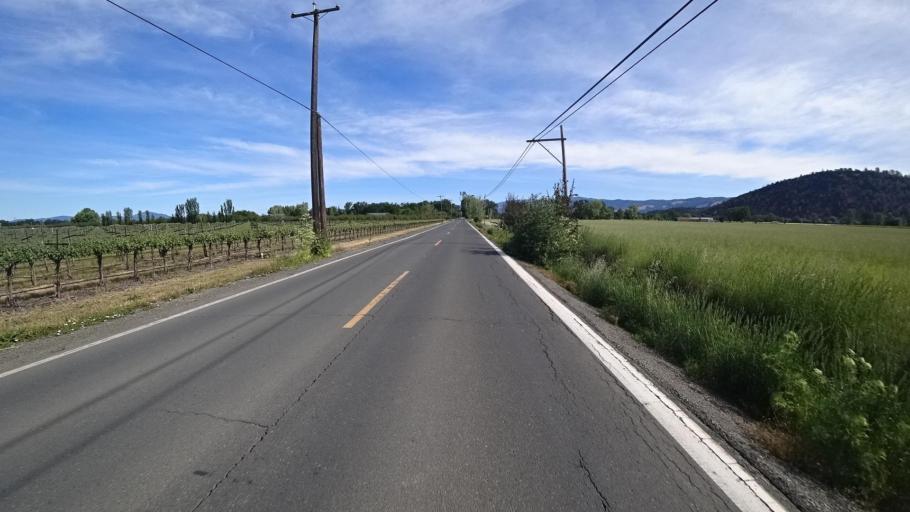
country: US
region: California
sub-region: Lake County
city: Kelseyville
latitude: 38.9945
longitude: -122.8290
